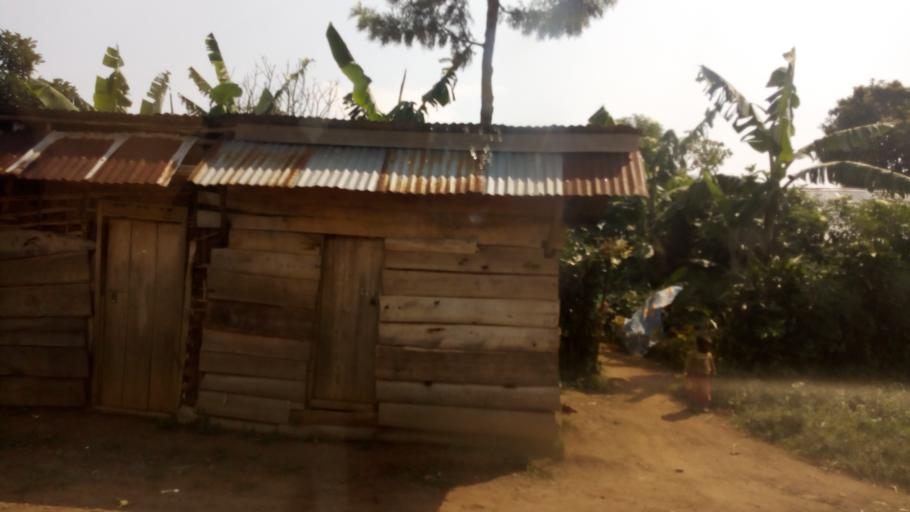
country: UG
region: Western Region
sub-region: Kanungu District
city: Ntungamo
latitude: -1.0196
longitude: 29.5835
